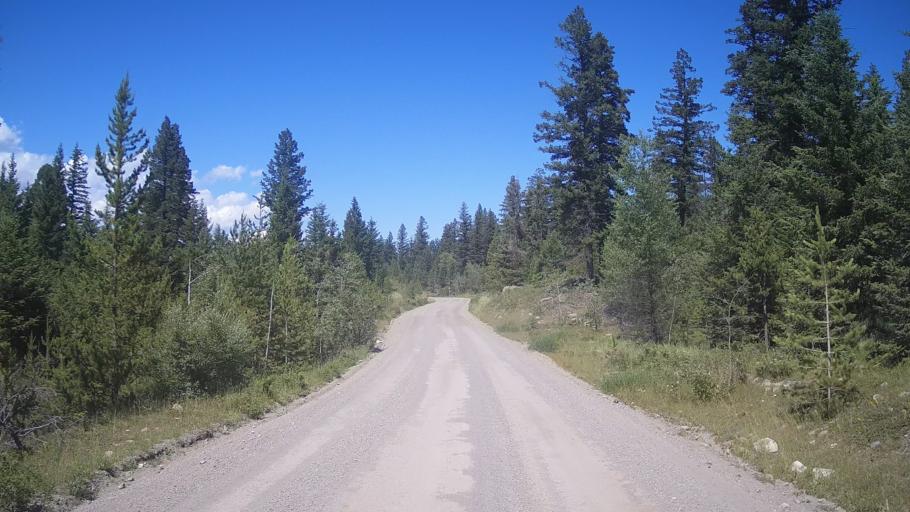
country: CA
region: British Columbia
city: Cache Creek
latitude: 51.1570
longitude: -121.5501
